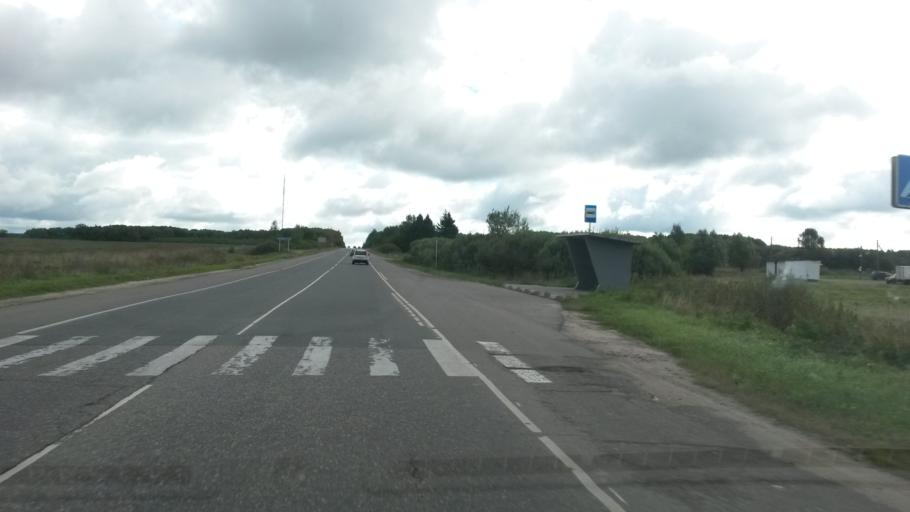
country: RU
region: Ivanovo
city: Rodniki
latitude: 57.0883
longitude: 41.6564
